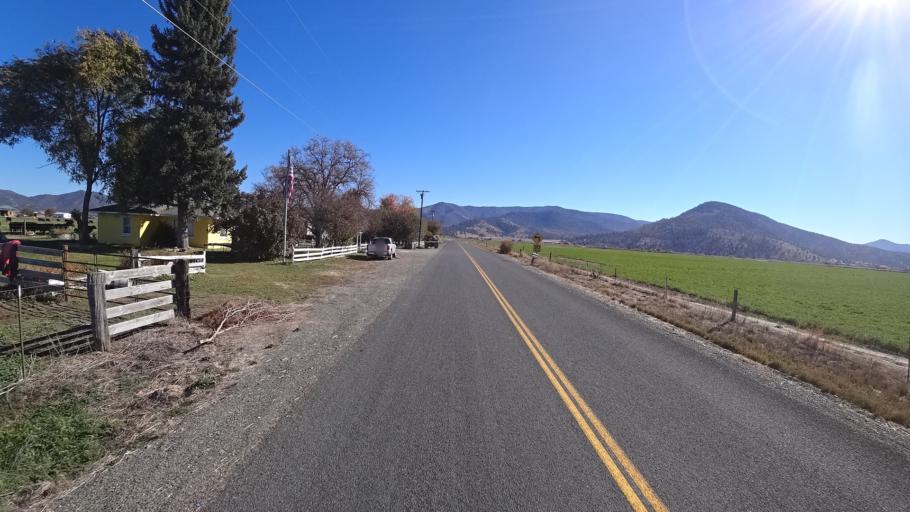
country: US
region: California
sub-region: Siskiyou County
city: Yreka
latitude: 41.5413
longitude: -122.8558
